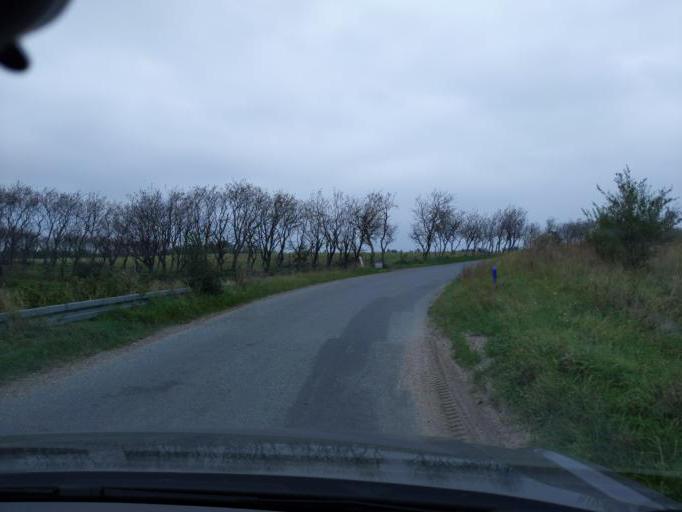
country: DK
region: Central Jutland
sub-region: Viborg Kommune
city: Stoholm
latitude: 56.5035
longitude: 9.2468
